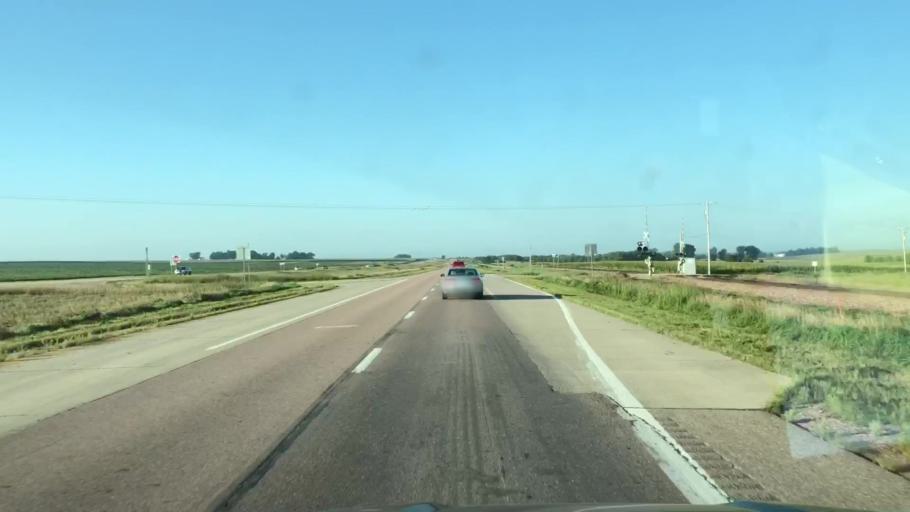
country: US
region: Iowa
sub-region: O'Brien County
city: Sheldon
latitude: 43.1280
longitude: -95.8845
